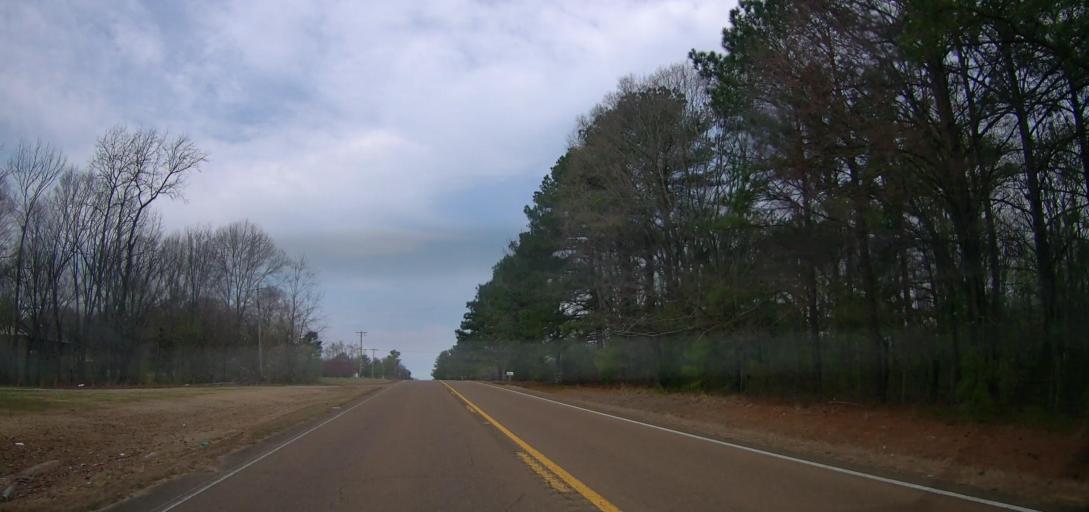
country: US
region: Mississippi
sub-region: Marshall County
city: Byhalia
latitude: 34.8384
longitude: -89.5950
